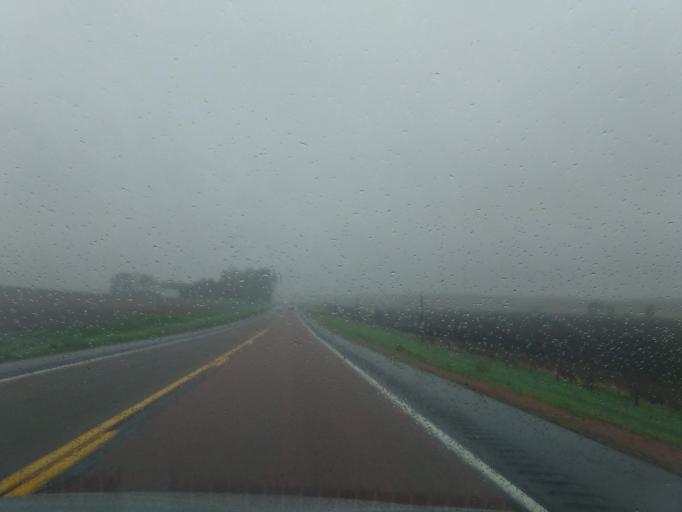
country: US
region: Nebraska
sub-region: Wayne County
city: Wayne
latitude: 42.2357
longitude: -97.1010
